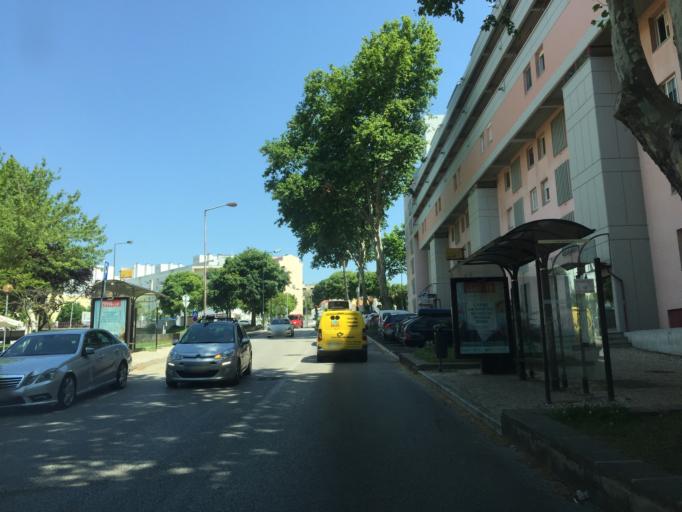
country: PT
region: Lisbon
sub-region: Odivelas
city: Olival do Basto
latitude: 38.7623
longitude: -9.1707
